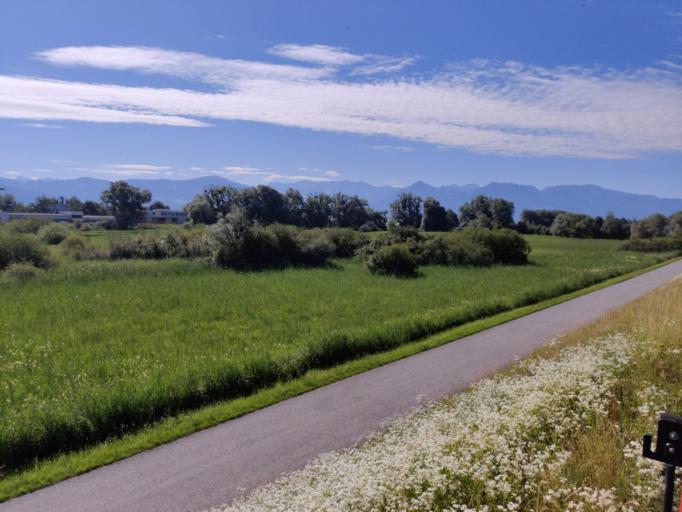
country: AT
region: Vorarlberg
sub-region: Politischer Bezirk Bregenz
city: Fussach
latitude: 47.4823
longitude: 9.6715
